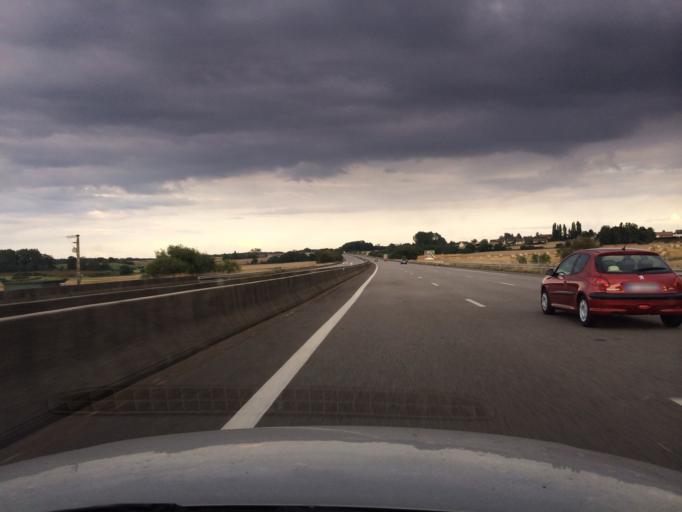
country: FR
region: Haute-Normandie
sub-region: Departement de l'Eure
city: Ande
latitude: 49.1693
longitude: 1.2516
